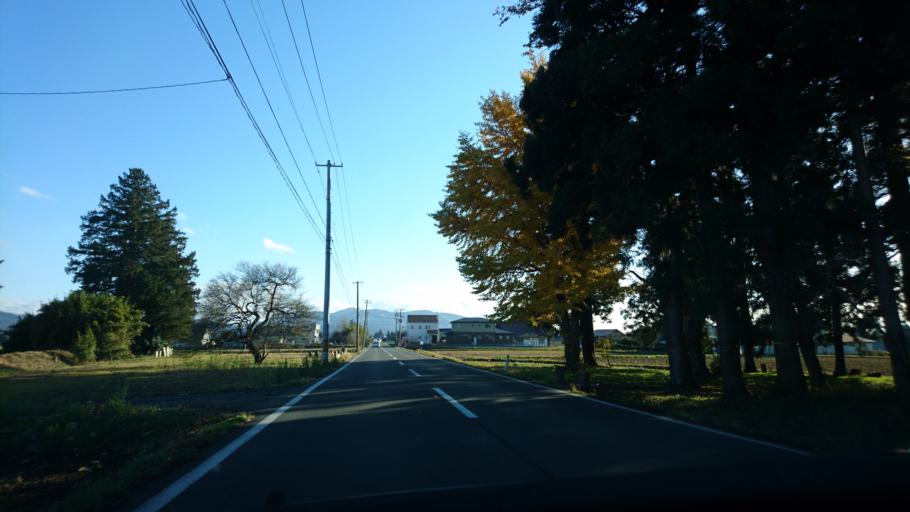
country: JP
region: Iwate
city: Mizusawa
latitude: 39.1030
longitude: 141.1571
